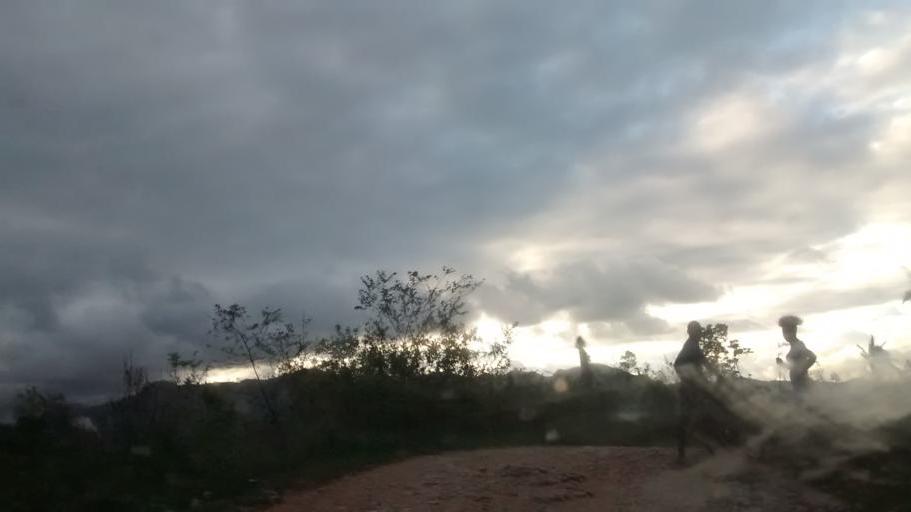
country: HT
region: Grandans
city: Corail
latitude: 18.4760
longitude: -73.7963
